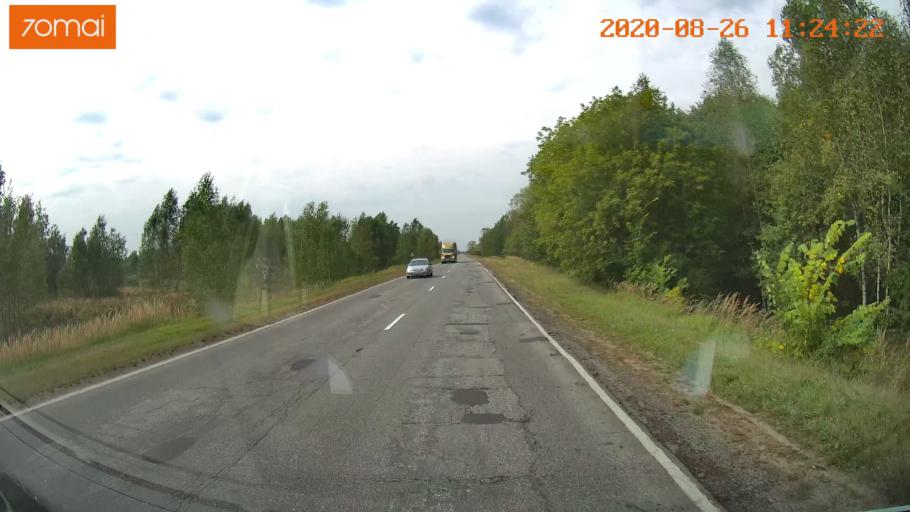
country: RU
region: Rjazan
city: Shilovo
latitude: 54.3470
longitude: 40.9887
